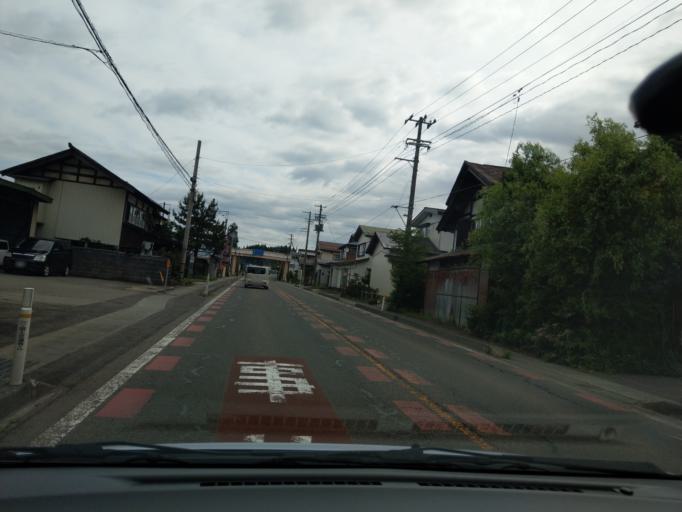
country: JP
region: Akita
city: Yokotemachi
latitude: 39.3682
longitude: 140.5677
